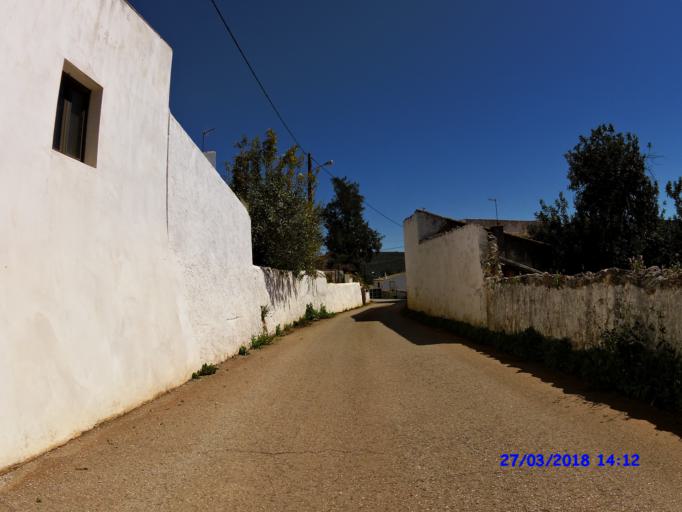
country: PT
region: Faro
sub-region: Loule
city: Boliqueime
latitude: 37.2092
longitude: -8.1712
